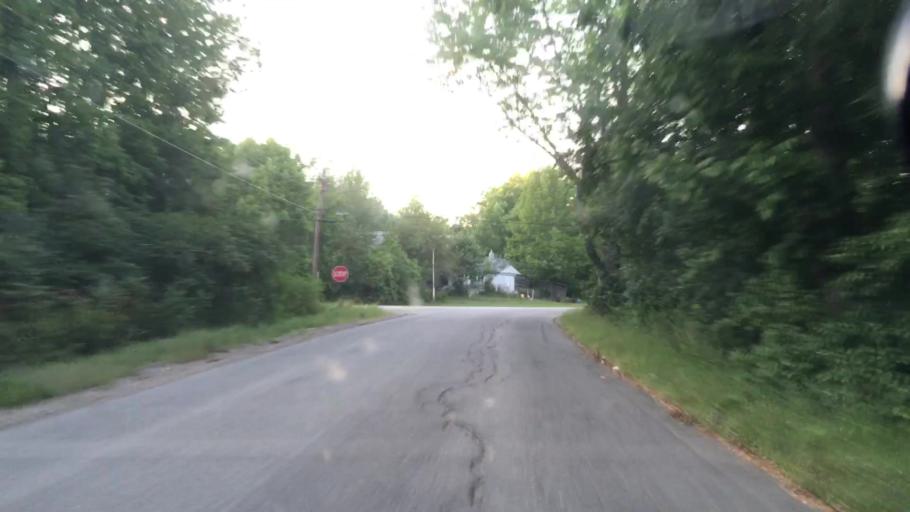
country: US
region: Maine
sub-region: Waldo County
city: Frankfort
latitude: 44.6714
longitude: -68.9262
